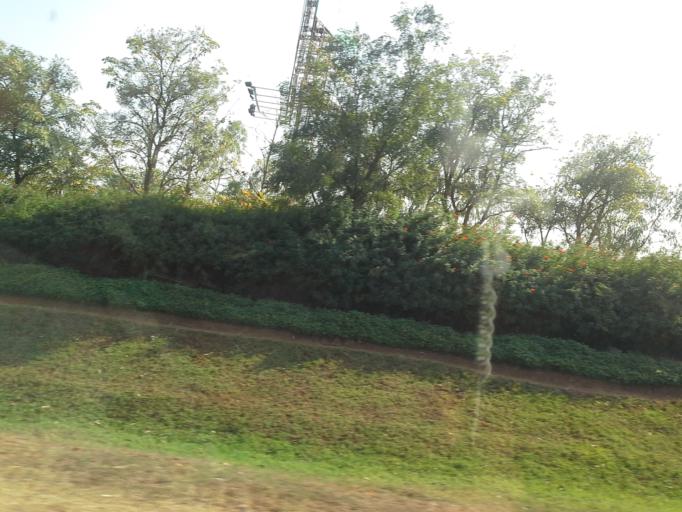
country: IN
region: Telangana
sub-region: Rangareddi
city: Balapur
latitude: 17.2451
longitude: 78.4007
